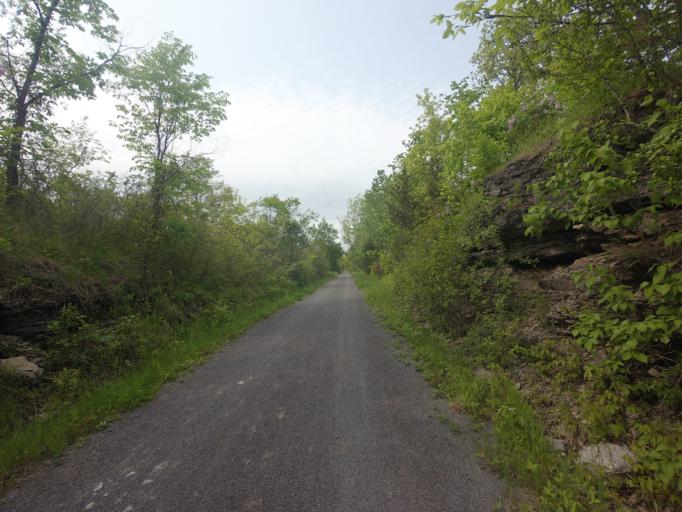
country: CA
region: Ontario
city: Kingston
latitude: 44.3227
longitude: -76.5876
